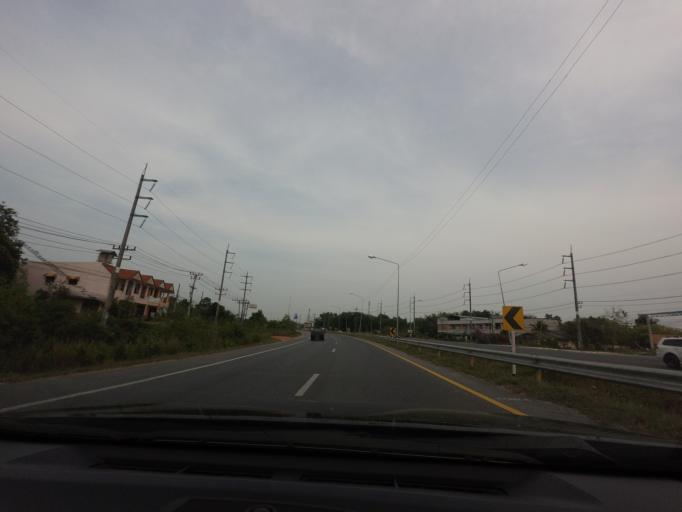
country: TH
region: Songkhla
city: Chana
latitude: 6.9175
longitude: 100.7278
